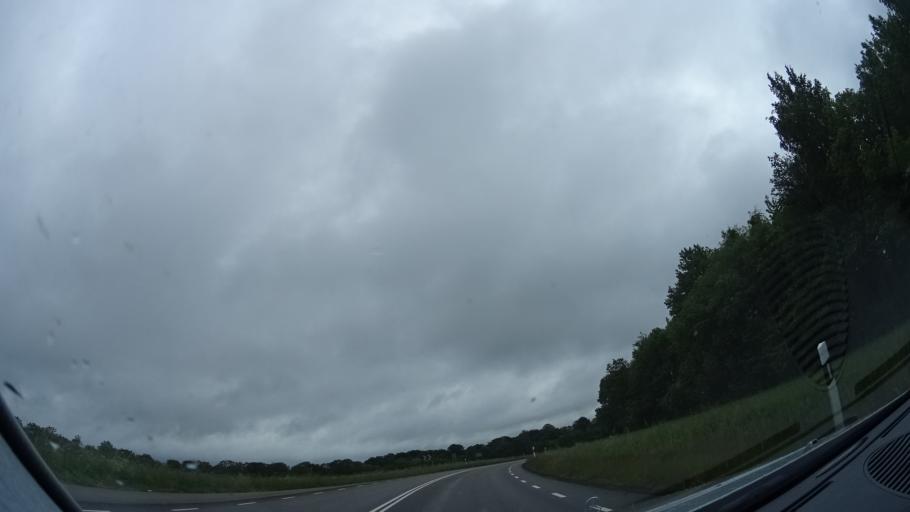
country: SE
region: Skane
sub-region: Hoors Kommun
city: Satofta
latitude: 55.8799
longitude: 13.5102
